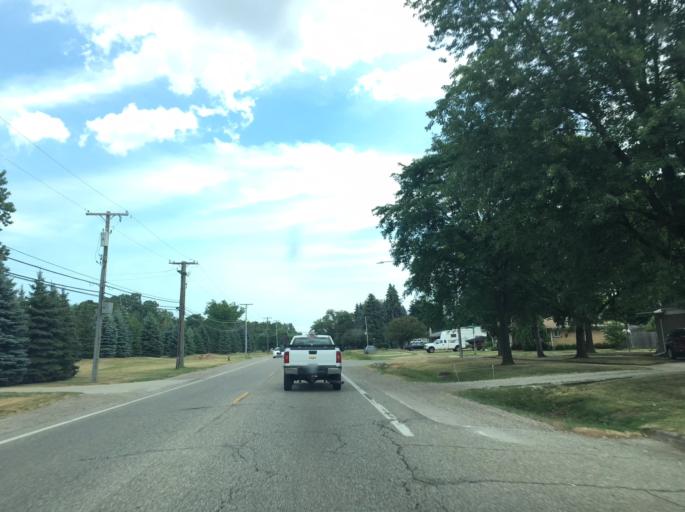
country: US
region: Michigan
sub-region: Macomb County
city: Sterling Heights
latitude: 42.6007
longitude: -83.0215
